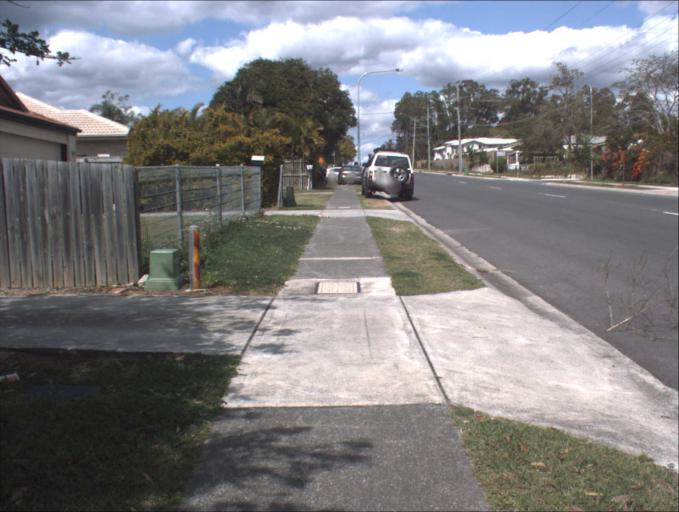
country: AU
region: Queensland
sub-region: Logan
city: Logan City
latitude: -27.6754
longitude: 153.0941
